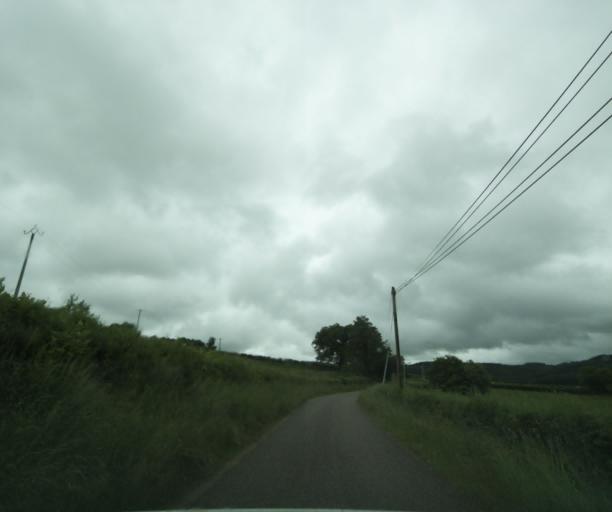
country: FR
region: Bourgogne
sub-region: Departement de Saone-et-Loire
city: Matour
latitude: 46.4574
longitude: 4.4531
